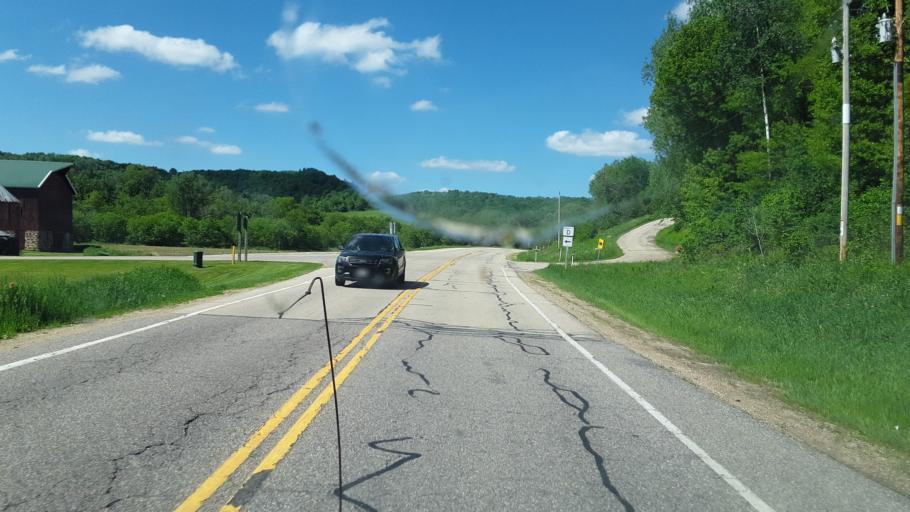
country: US
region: Wisconsin
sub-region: Richland County
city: Richland Center
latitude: 43.4355
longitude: -90.2429
